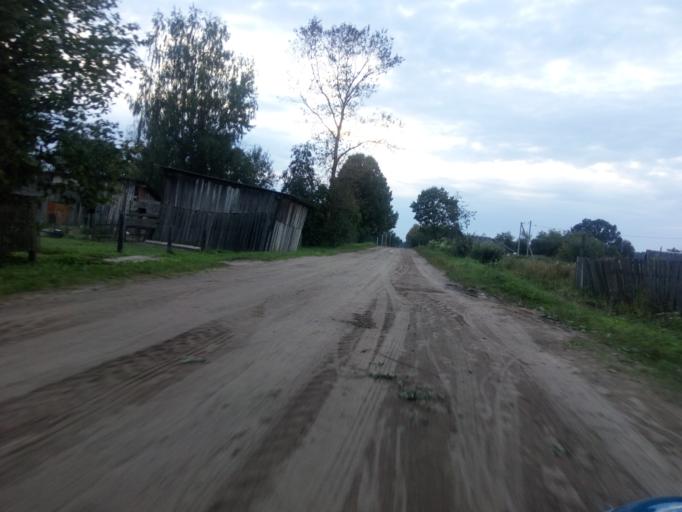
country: BY
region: Vitebsk
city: Dzisna
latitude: 55.6703
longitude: 28.3178
